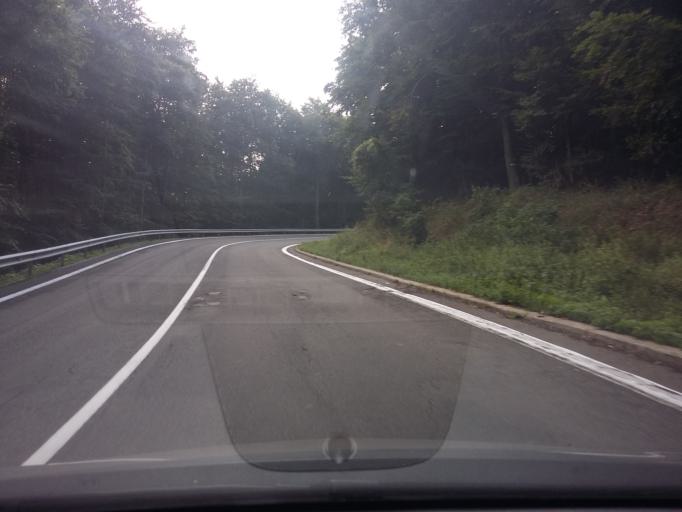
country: SK
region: Bratislavsky
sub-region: Okres Pezinok
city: Pezinok
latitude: 48.3491
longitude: 17.2143
